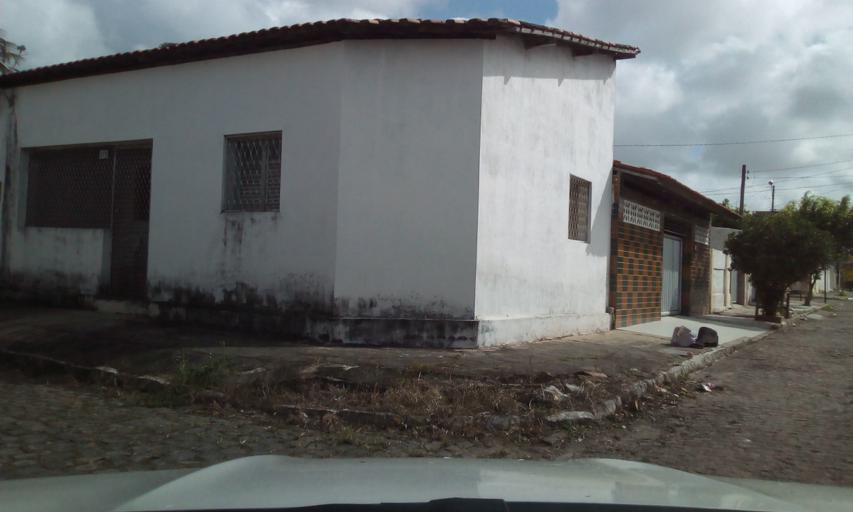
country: BR
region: Paraiba
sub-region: Joao Pessoa
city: Joao Pessoa
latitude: -7.1120
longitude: -34.8797
